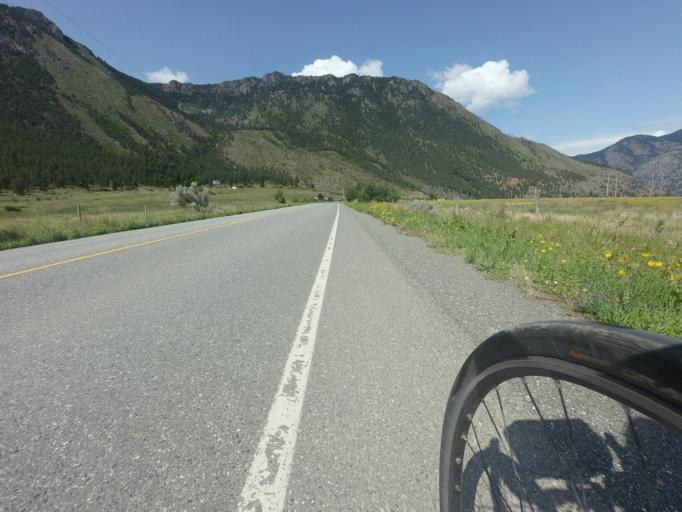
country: CA
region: British Columbia
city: Lillooet
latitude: 50.7422
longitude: -121.8781
